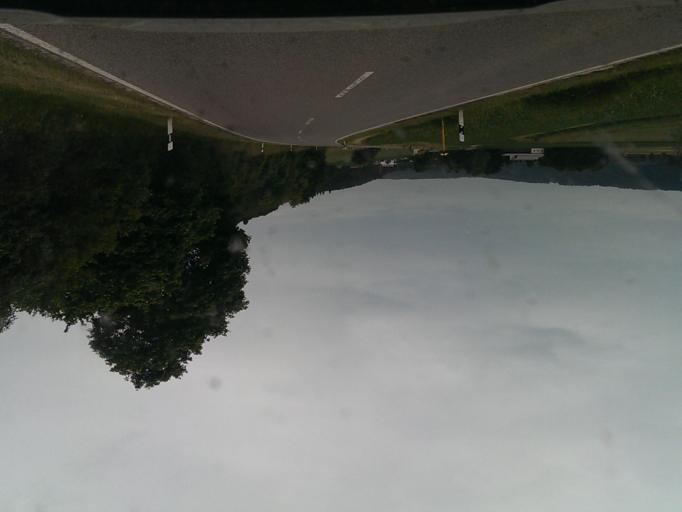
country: DE
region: Bavaria
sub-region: Upper Palatinate
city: Berching
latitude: 49.0283
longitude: 11.4516
